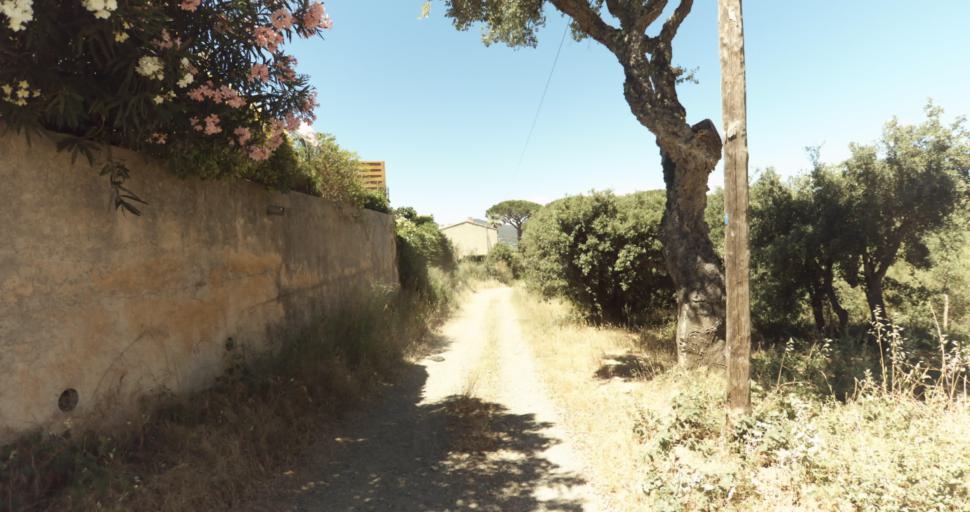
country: FR
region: Provence-Alpes-Cote d'Azur
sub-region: Departement du Var
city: Gassin
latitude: 43.2558
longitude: 6.5657
